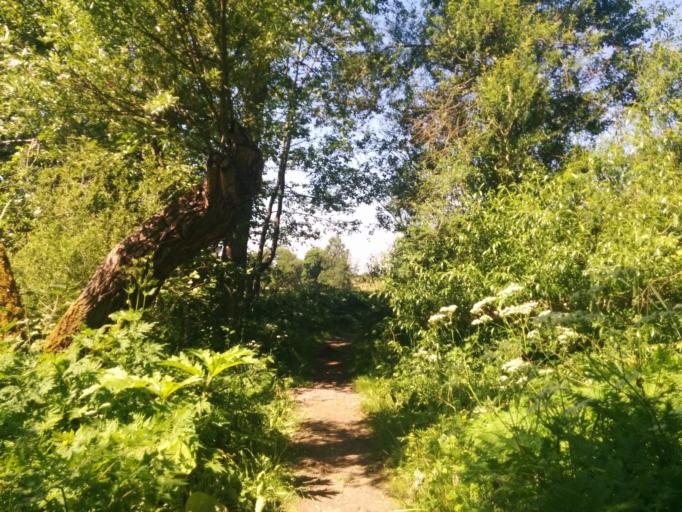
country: SE
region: Skane
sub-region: Lunds Kommun
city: Genarp
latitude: 55.5860
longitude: 13.3852
